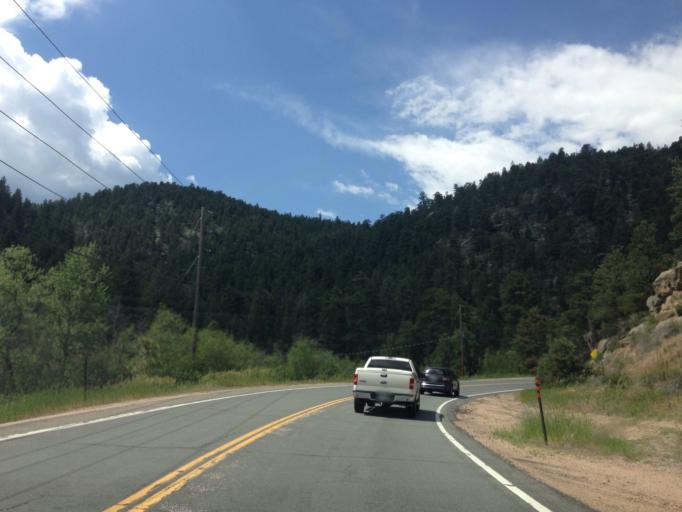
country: US
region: Colorado
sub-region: Larimer County
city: Estes Park
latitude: 40.3901
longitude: -105.4500
